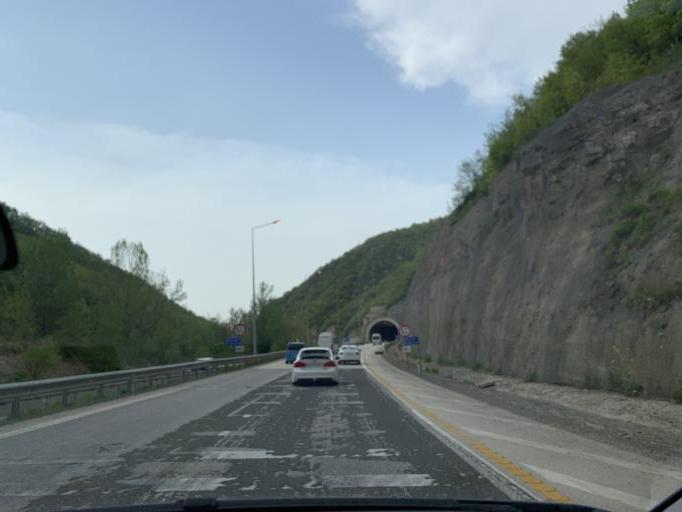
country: TR
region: Bursa
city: Kursunlu
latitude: 40.0037
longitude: 29.6520
